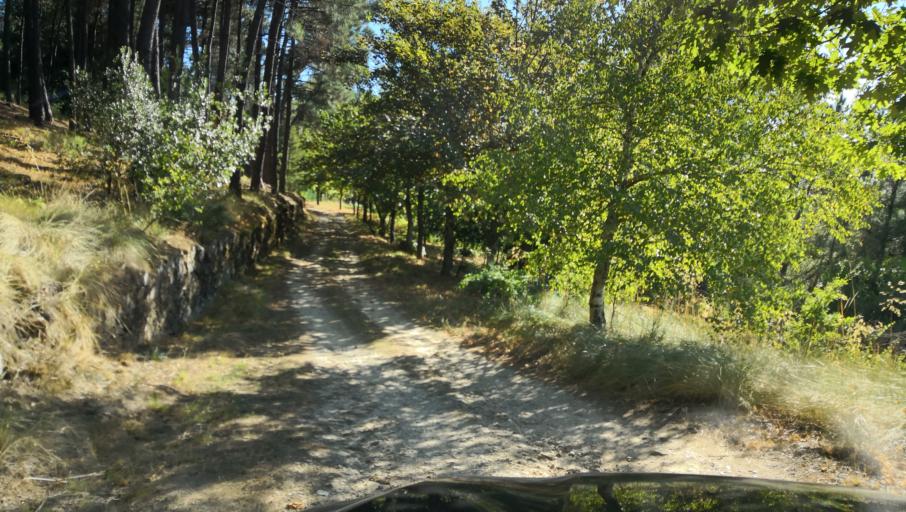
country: PT
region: Vila Real
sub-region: Vila Real
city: Vila Real
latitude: 41.2904
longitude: -7.7414
